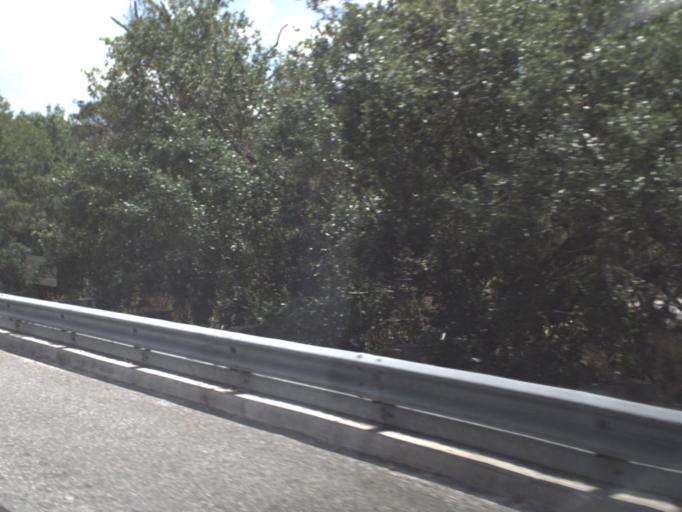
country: US
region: Florida
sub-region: Orange County
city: Wedgefield
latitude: 28.4515
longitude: -81.0955
